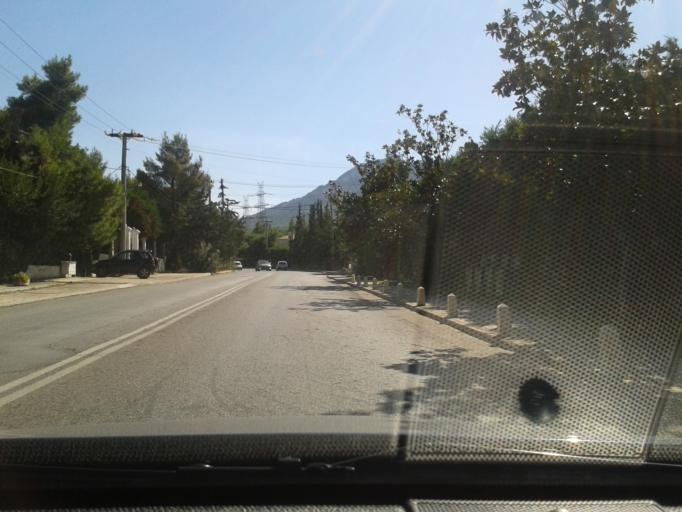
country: GR
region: Attica
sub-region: Nomarchia Anatolikis Attikis
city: Drosia
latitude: 38.1124
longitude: 23.8535
